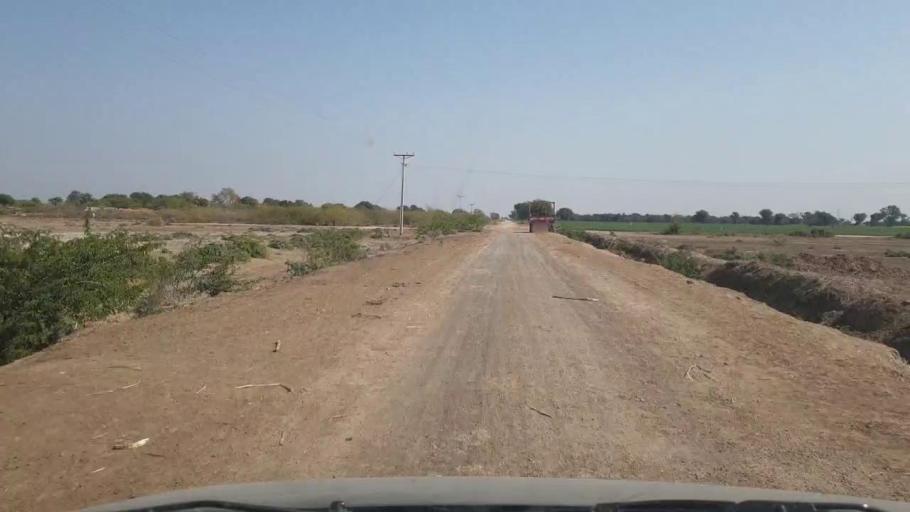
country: PK
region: Sindh
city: Samaro
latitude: 25.1582
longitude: 69.3270
